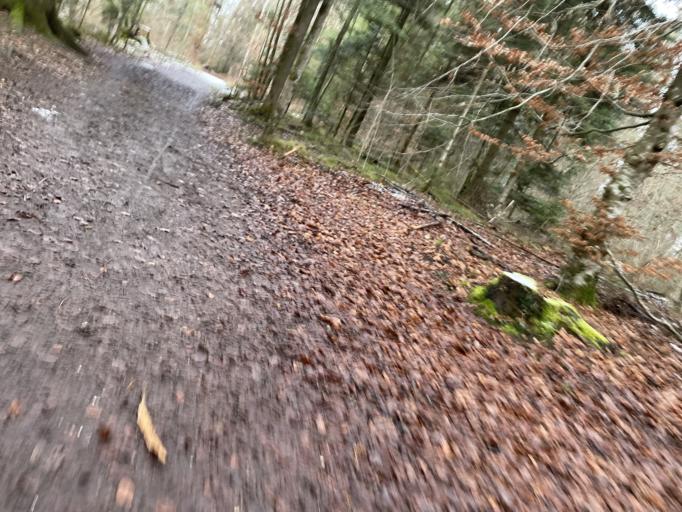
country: CH
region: Bern
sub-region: Thun District
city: Uttigen
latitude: 46.8091
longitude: 7.5692
